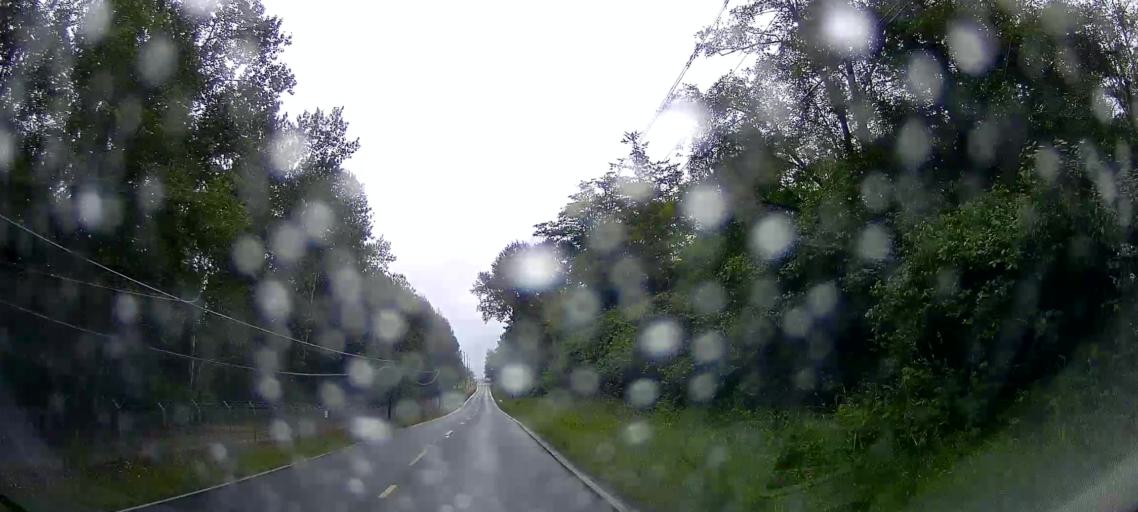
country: US
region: Washington
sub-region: Whatcom County
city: Ferndale
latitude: 48.8195
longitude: -122.6883
